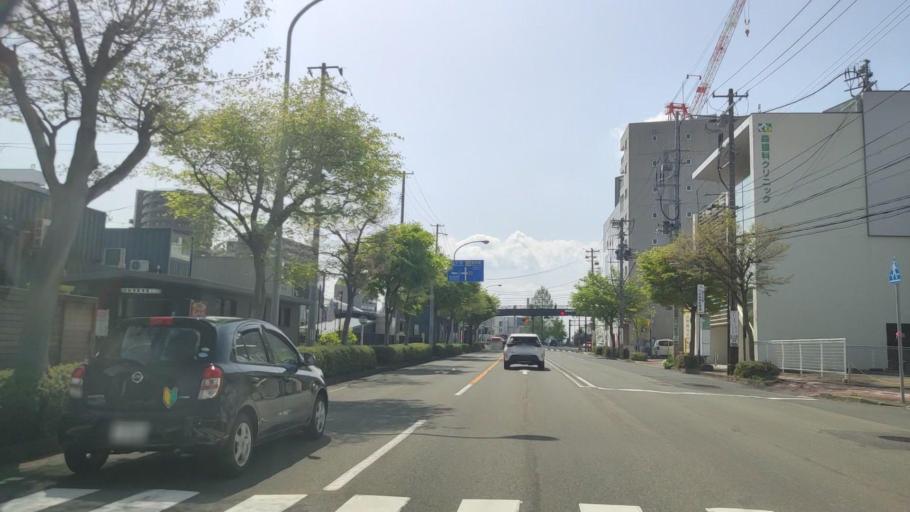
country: JP
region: Iwate
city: Morioka-shi
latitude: 39.7033
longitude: 141.1383
